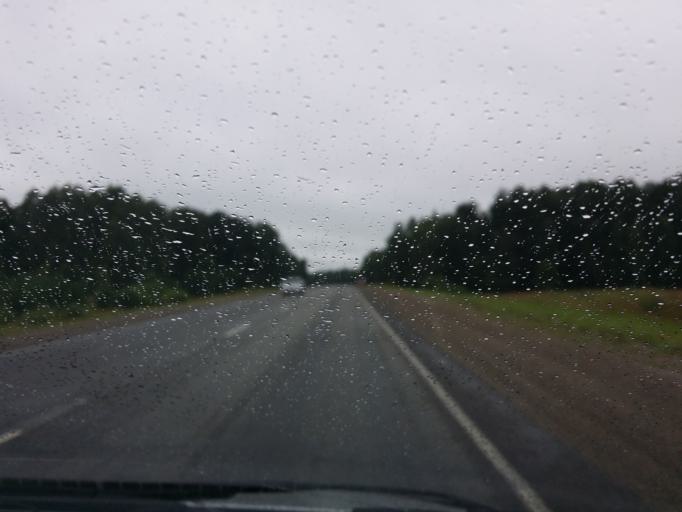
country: RU
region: Altai Krai
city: Troitskoye
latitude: 53.0469
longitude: 84.6905
